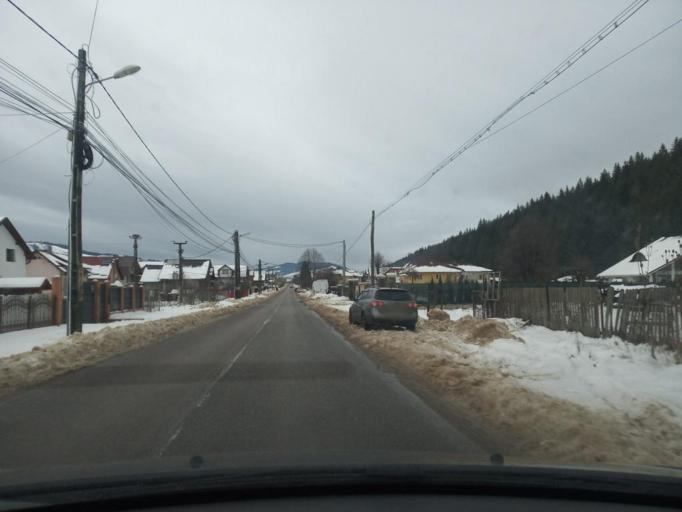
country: RO
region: Suceava
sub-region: Oras Gura Humorului
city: Gura Humorului
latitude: 47.5711
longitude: 25.8815
